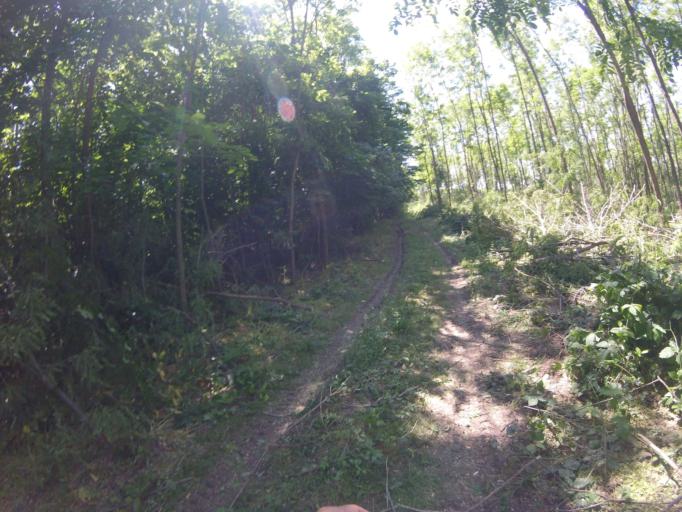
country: HU
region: Zala
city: Zalaszentgrot
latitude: 46.9128
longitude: 17.0418
